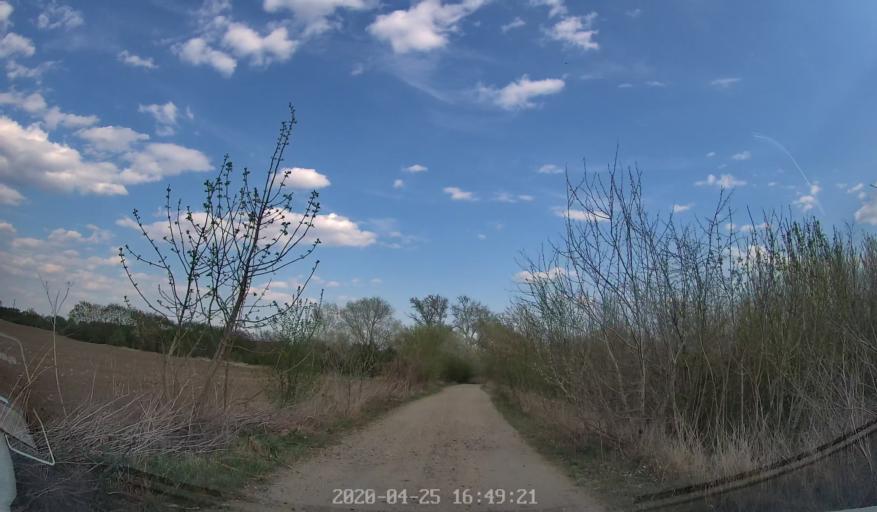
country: MD
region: Chisinau
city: Vadul lui Voda
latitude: 47.1293
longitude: 29.0822
